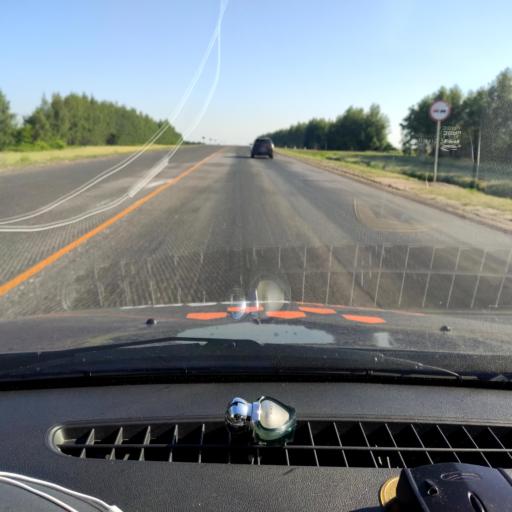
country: RU
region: Orjol
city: Zmiyevka
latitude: 52.7636
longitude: 36.3215
